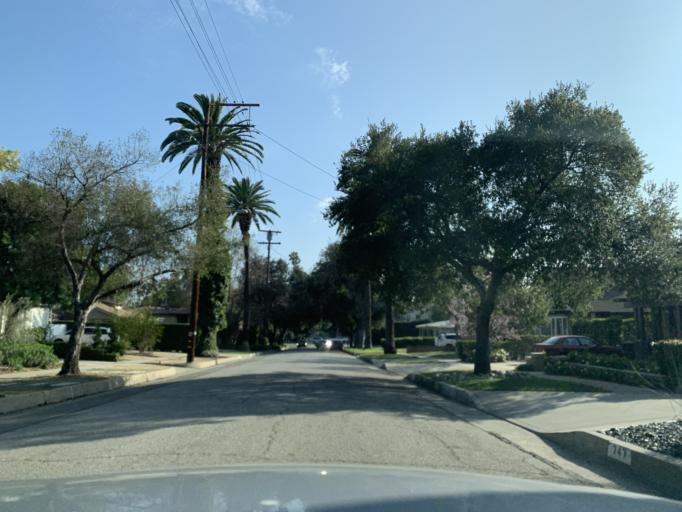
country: US
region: California
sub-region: Los Angeles County
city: Pasadena
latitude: 34.1591
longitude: -118.1231
